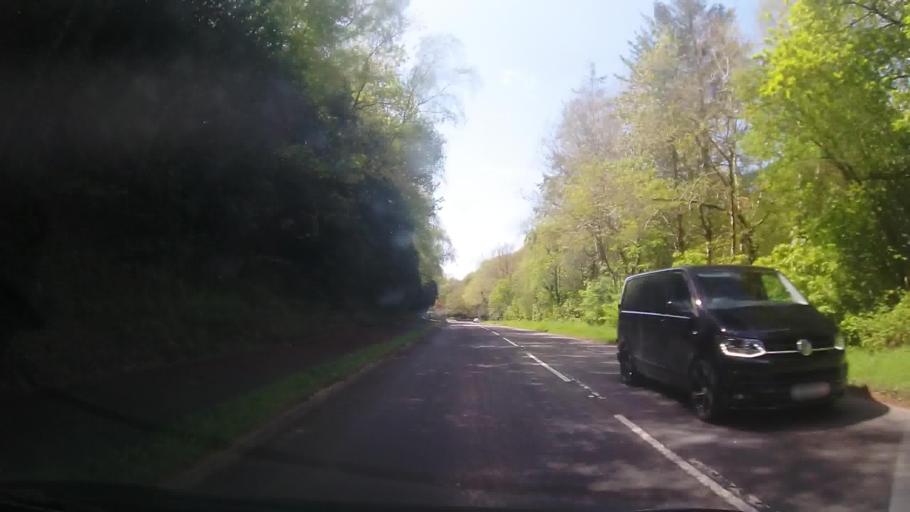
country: GB
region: Wales
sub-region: Gwynedd
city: Porthmadog
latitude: 52.9347
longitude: -4.1682
